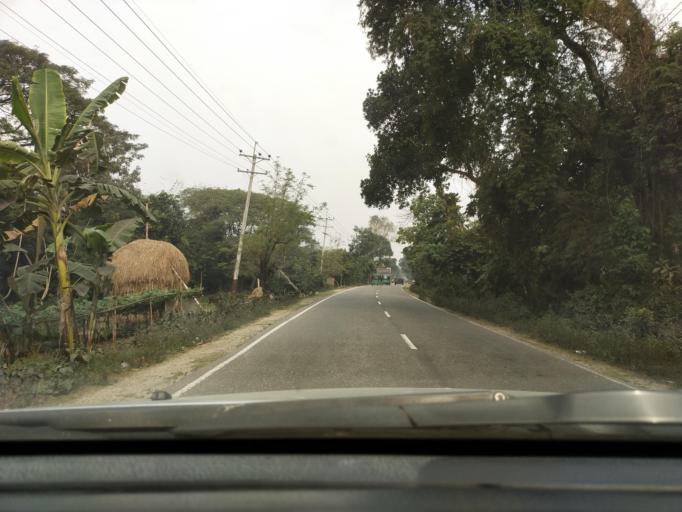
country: BD
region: Dhaka
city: Narsingdi
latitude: 24.0144
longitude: 90.7372
